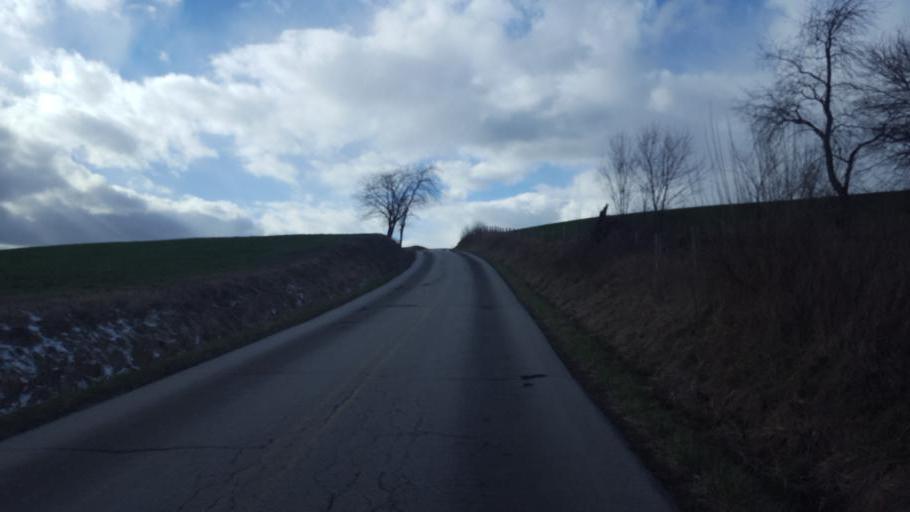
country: US
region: Ohio
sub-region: Tuscarawas County
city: Sugarcreek
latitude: 40.5013
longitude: -81.7279
